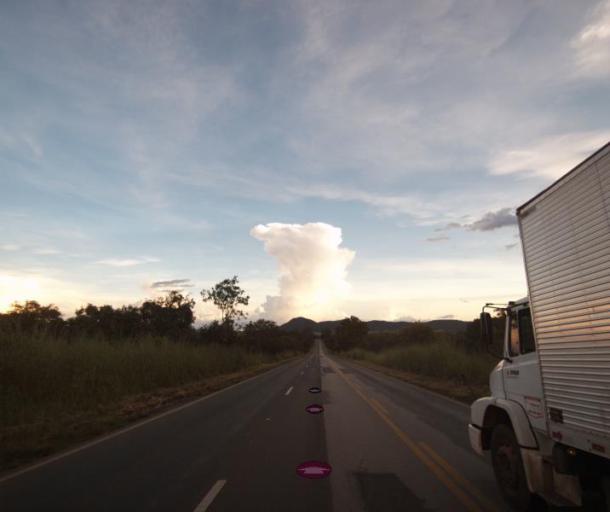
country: BR
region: Goias
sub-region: Uruacu
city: Uruacu
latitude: -14.3463
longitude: -49.1573
